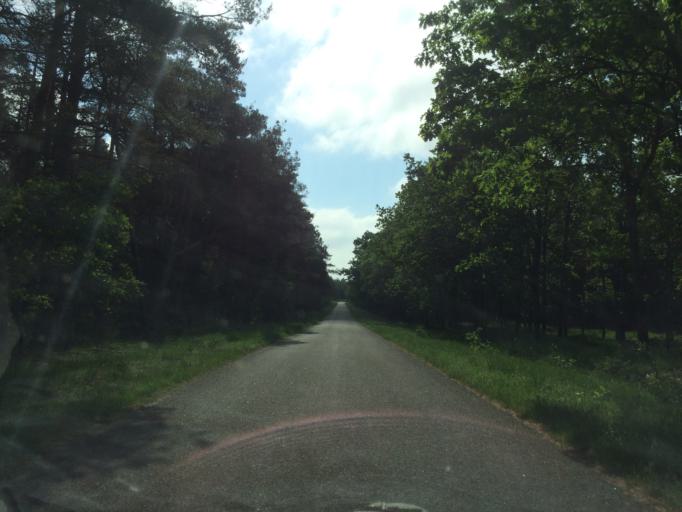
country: DK
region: Central Jutland
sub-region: Holstebro Kommune
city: Ulfborg
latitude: 56.2186
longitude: 8.4519
